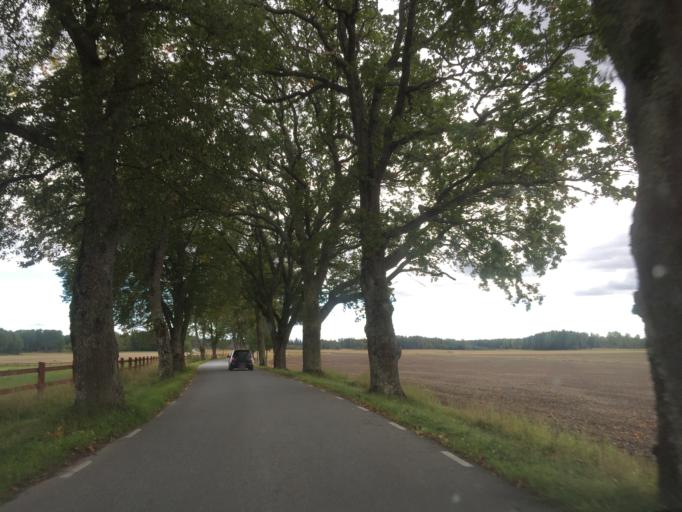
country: SE
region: OErebro
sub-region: Orebro Kommun
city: Hovsta
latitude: 59.3457
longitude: 15.1690
